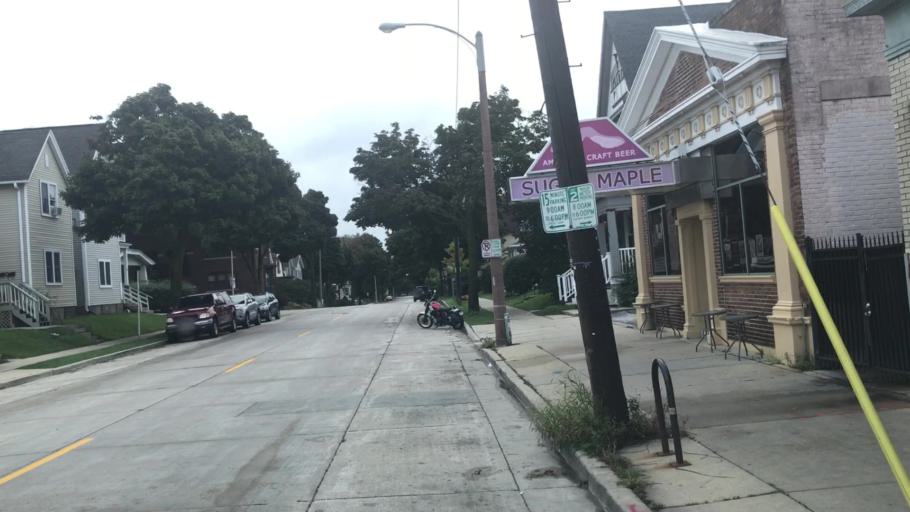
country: US
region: Wisconsin
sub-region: Milwaukee County
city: Milwaukee
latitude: 43.0029
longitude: -87.9037
